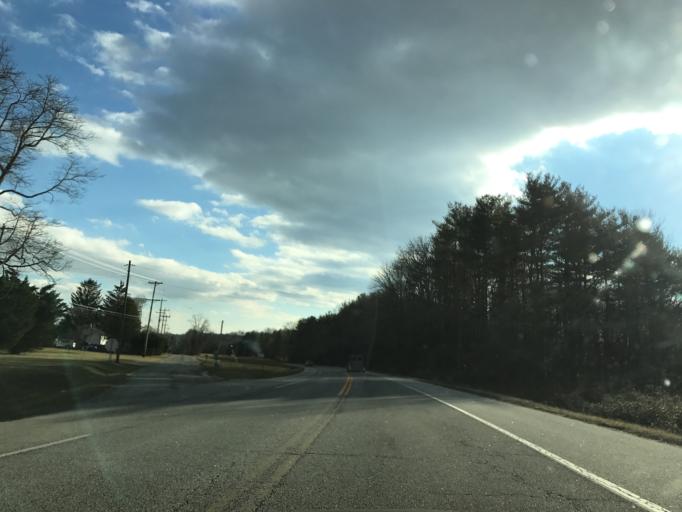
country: US
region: Maryland
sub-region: Cecil County
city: Rising Sun
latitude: 39.6666
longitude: -76.0755
